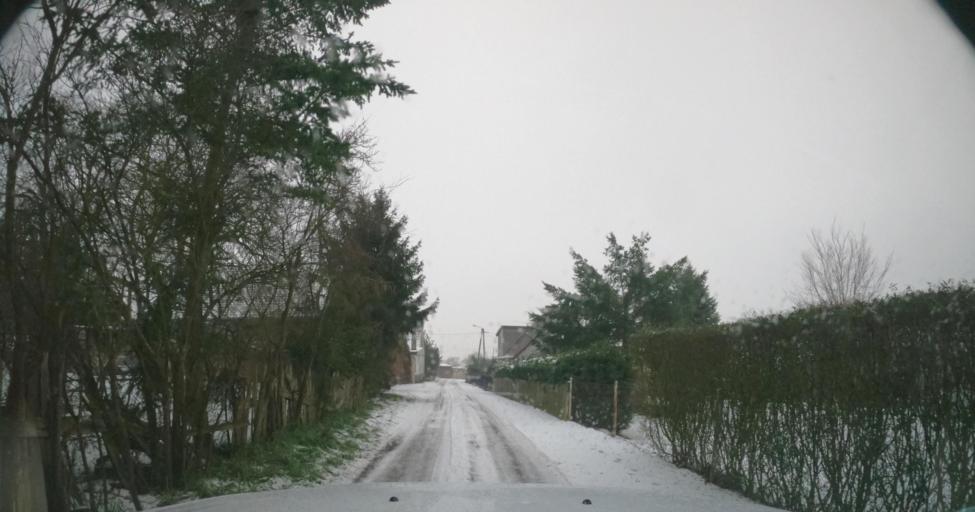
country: PL
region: West Pomeranian Voivodeship
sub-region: Powiat kamienski
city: Golczewo
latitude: 53.7884
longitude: 14.9538
